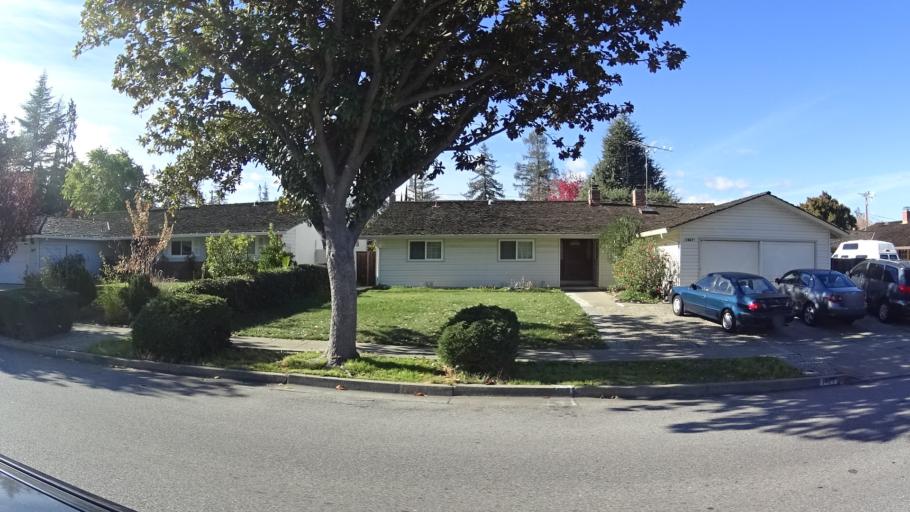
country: US
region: California
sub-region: Santa Clara County
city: Sunnyvale
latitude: 37.3455
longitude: -122.0415
